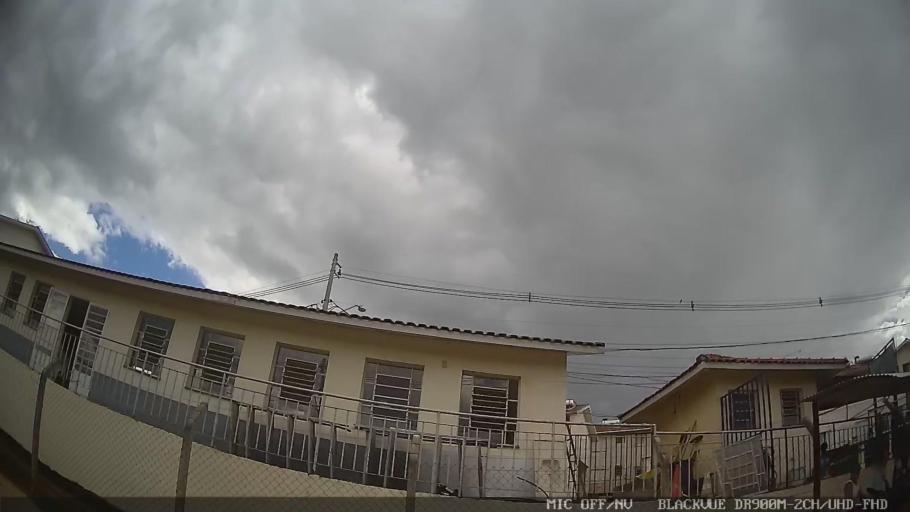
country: BR
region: Sao Paulo
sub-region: Jaguariuna
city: Jaguariuna
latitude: -22.6940
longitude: -46.9967
